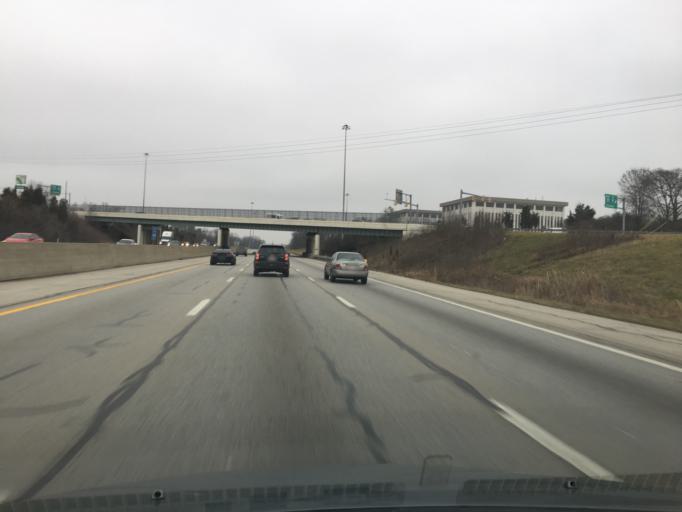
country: US
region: Ohio
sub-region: Hamilton County
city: Sharonville
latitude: 39.2886
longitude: -84.3973
